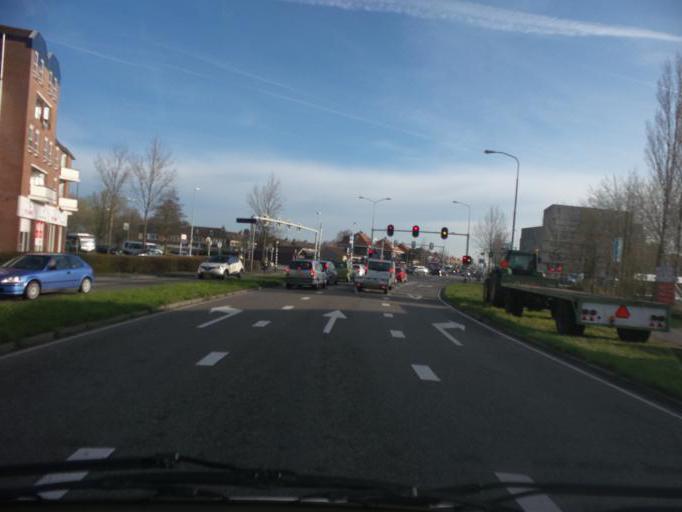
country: NL
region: South Holland
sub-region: Gemeente Gouda
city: Gouda
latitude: 52.0256
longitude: 4.7173
